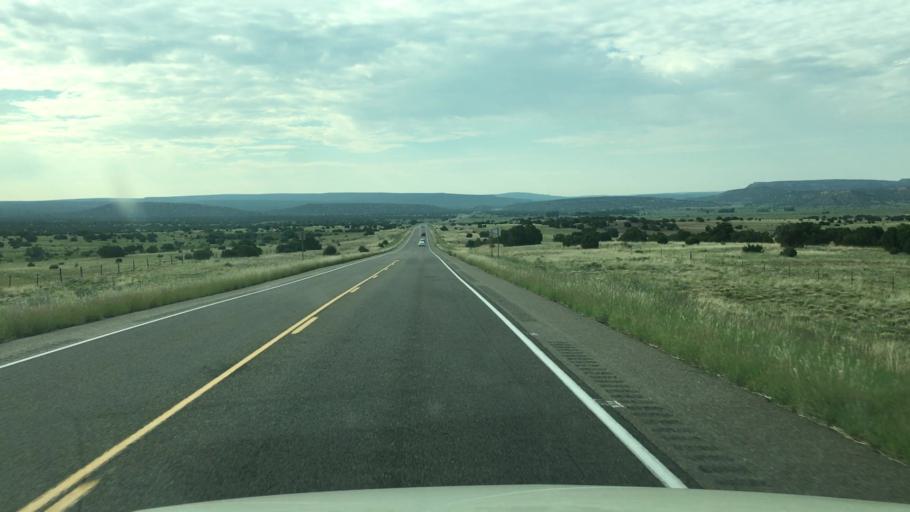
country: US
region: New Mexico
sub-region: Santa Fe County
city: Eldorado at Santa Fe
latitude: 35.4243
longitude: -105.8754
